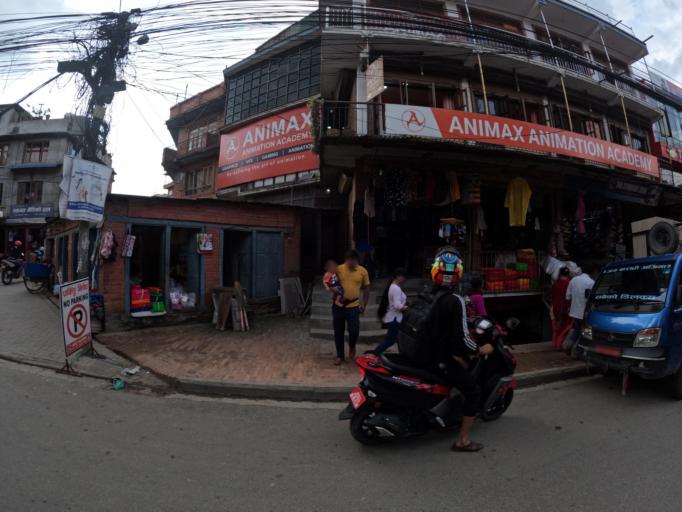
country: NP
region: Central Region
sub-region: Bagmati Zone
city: Bhaktapur
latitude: 27.6666
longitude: 85.4256
